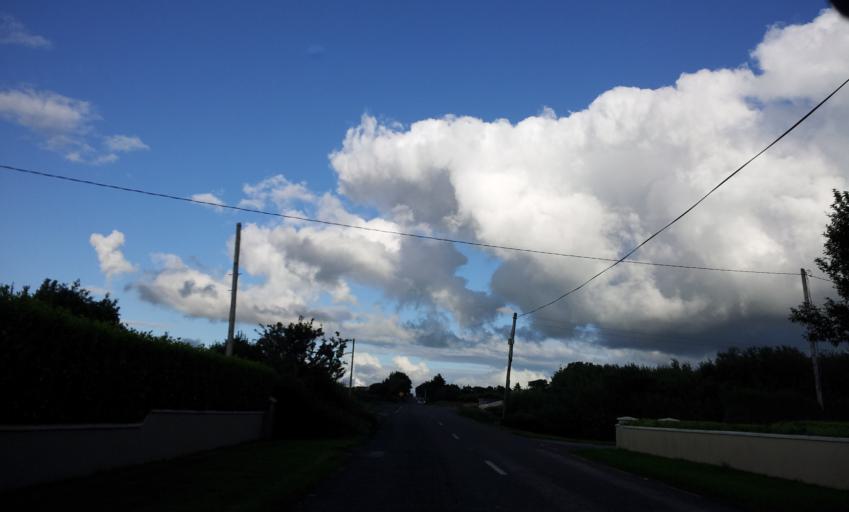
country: IE
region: Munster
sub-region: Ciarrai
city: Tralee
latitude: 52.2420
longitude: -9.7990
